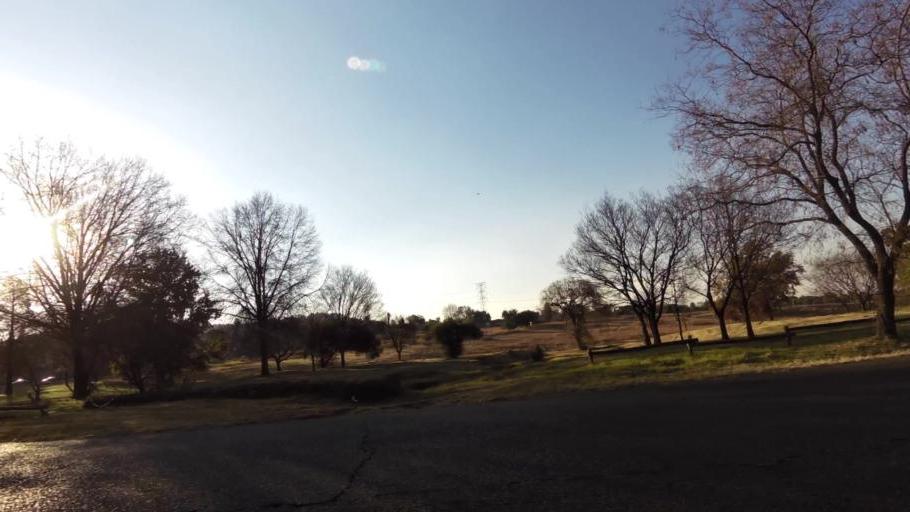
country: ZA
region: Gauteng
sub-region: City of Johannesburg Metropolitan Municipality
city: Johannesburg
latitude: -26.1583
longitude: 27.9808
